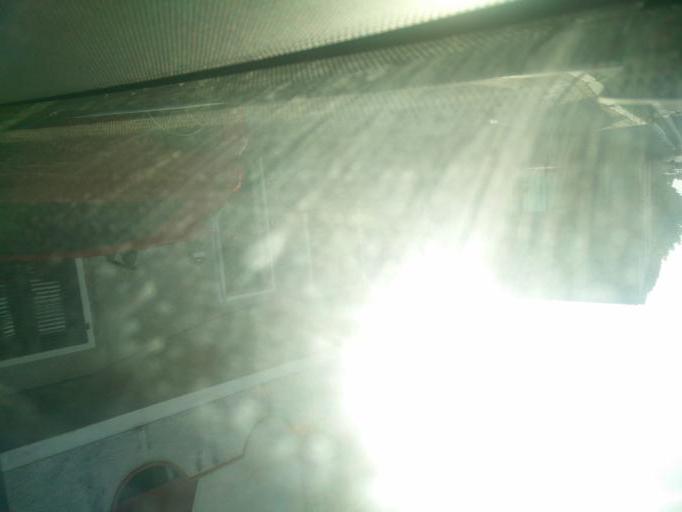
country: IT
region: Tuscany
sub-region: Provincia di Massa-Carrara
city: Massa
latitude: 44.0231
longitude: 10.1221
